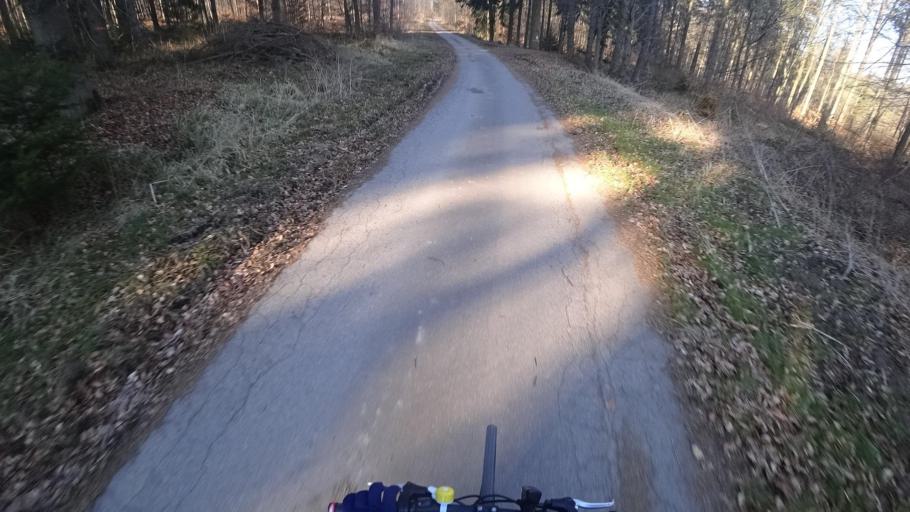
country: DE
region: Rheinland-Pfalz
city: Waldesch
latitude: 50.2531
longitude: 7.5271
